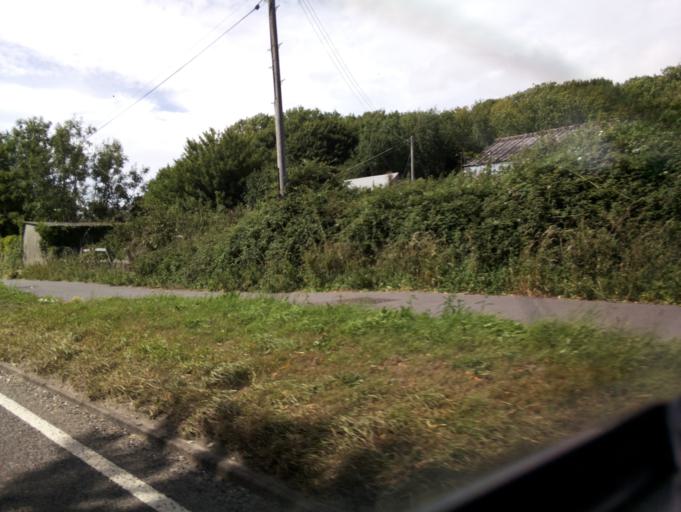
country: GB
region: England
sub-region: Dorset
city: Dorchester
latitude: 50.7378
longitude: -2.4786
